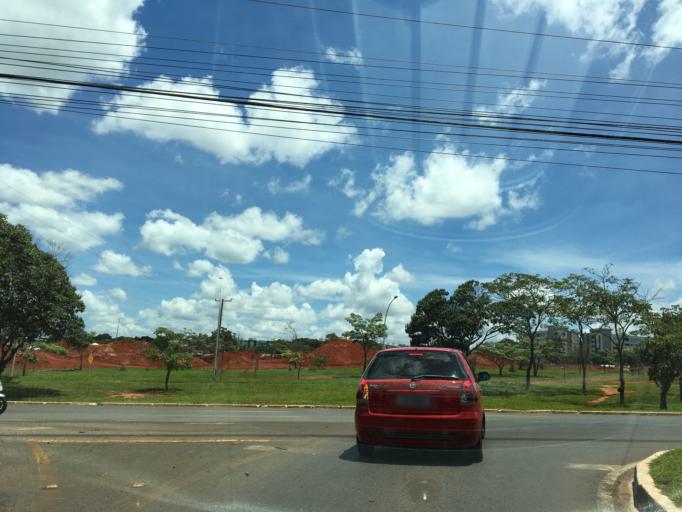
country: BR
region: Federal District
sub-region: Brasilia
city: Brasilia
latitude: -15.7321
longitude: -47.8957
